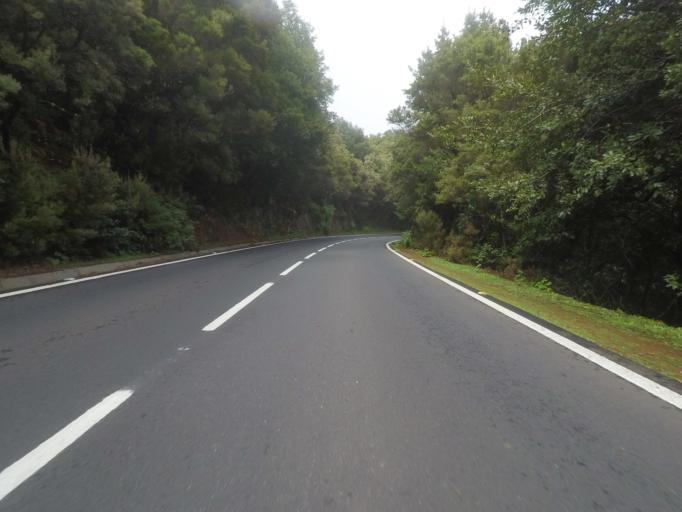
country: ES
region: Canary Islands
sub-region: Provincia de Santa Cruz de Tenerife
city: Alajero
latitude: 28.1106
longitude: -17.2412
